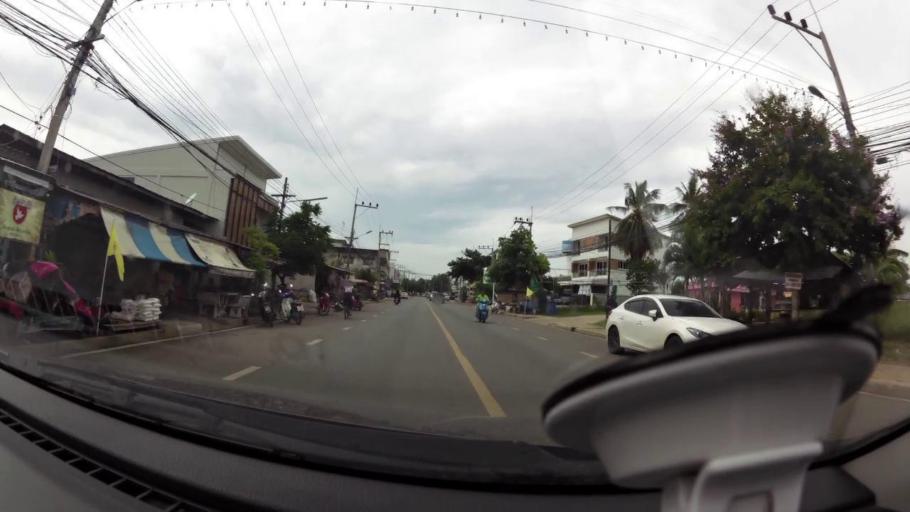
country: TH
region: Prachuap Khiri Khan
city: Pran Buri
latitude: 12.3918
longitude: 99.9870
